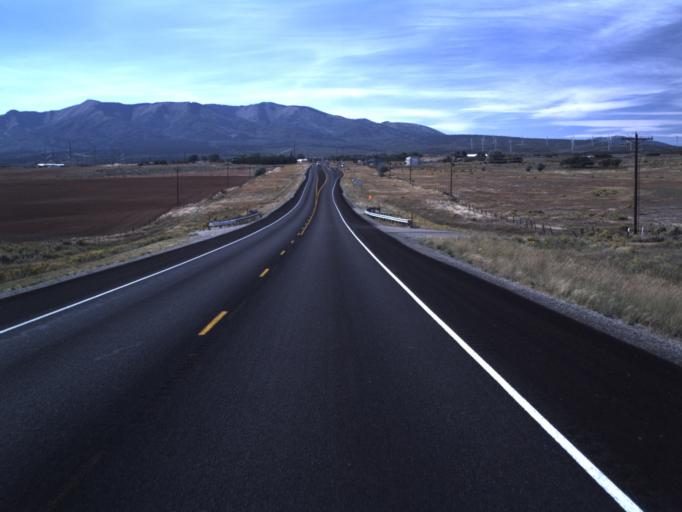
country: US
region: Utah
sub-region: San Juan County
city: Monticello
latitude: 37.8729
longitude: -109.2997
